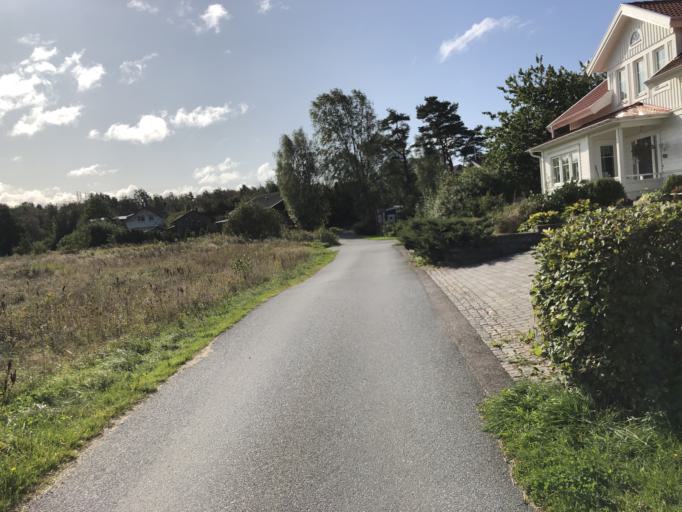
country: SE
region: Vaestra Goetaland
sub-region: Goteborg
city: Torslanda
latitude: 57.7353
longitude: 11.8169
